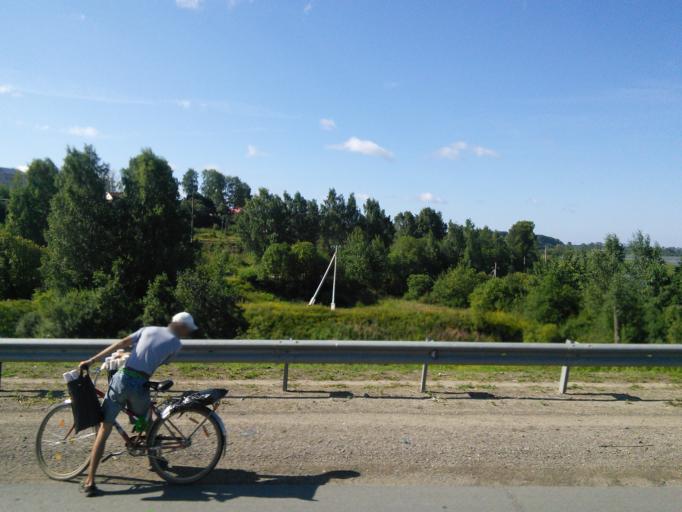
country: RU
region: Vologda
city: Sheksna
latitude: 59.2105
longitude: 38.4988
